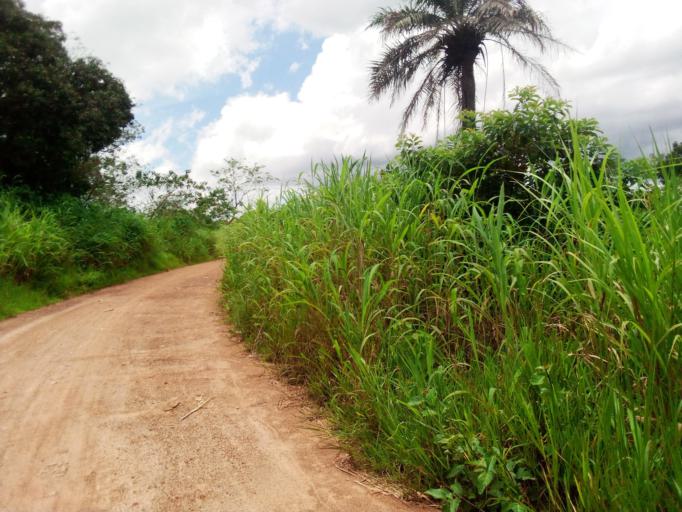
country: SL
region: Eastern Province
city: Simbakoro
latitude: 8.6037
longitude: -10.9850
